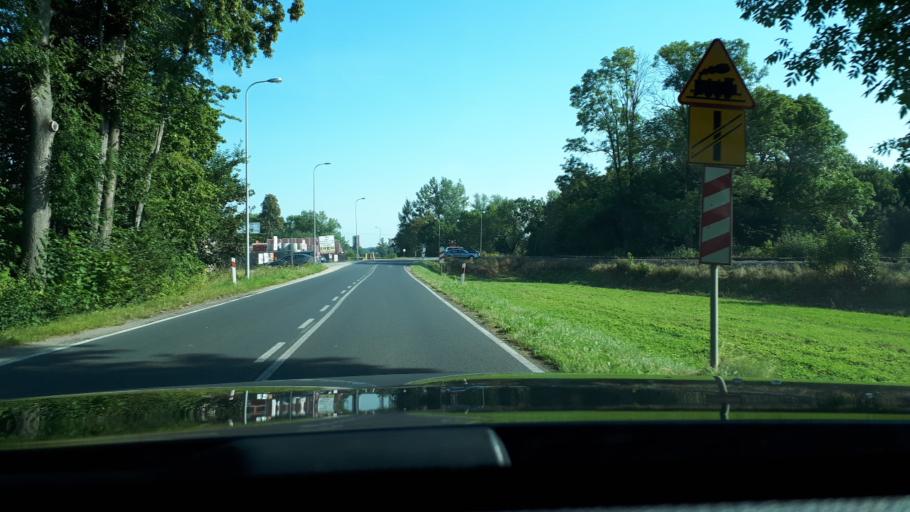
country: PL
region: Lower Silesian Voivodeship
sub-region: Powiat lubanski
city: Luban
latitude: 51.0749
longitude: 15.2945
